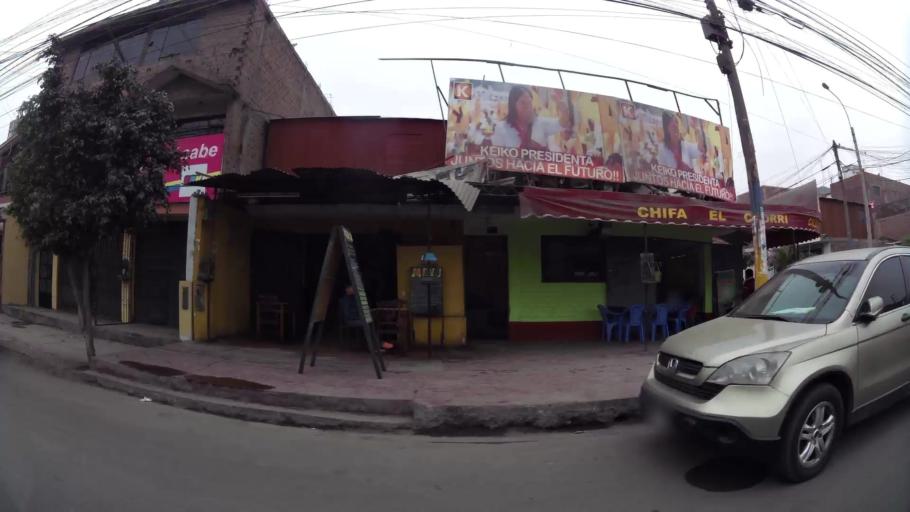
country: PE
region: Lima
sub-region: Lima
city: Independencia
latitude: -11.9890
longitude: -76.9964
